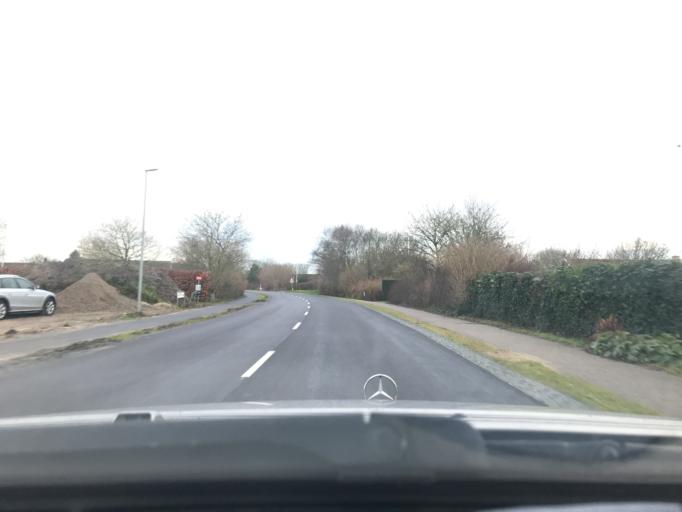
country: DK
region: South Denmark
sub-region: Esbjerg Kommune
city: Ribe
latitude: 55.3165
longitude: 8.7252
